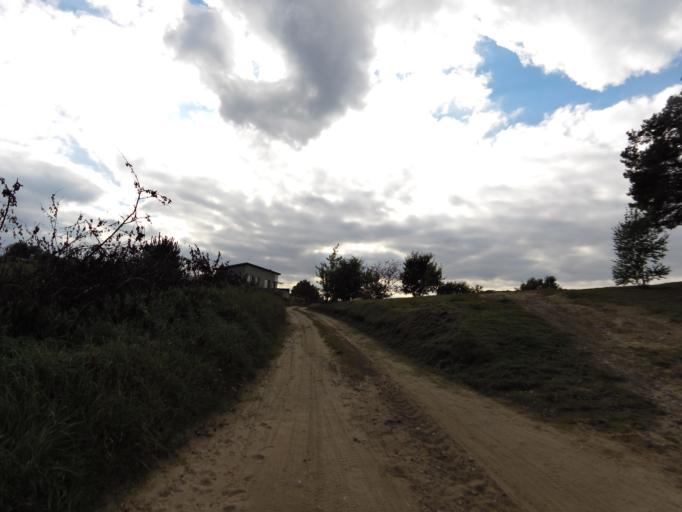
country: LT
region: Vilnius County
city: Pilaite
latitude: 54.7013
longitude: 25.1611
